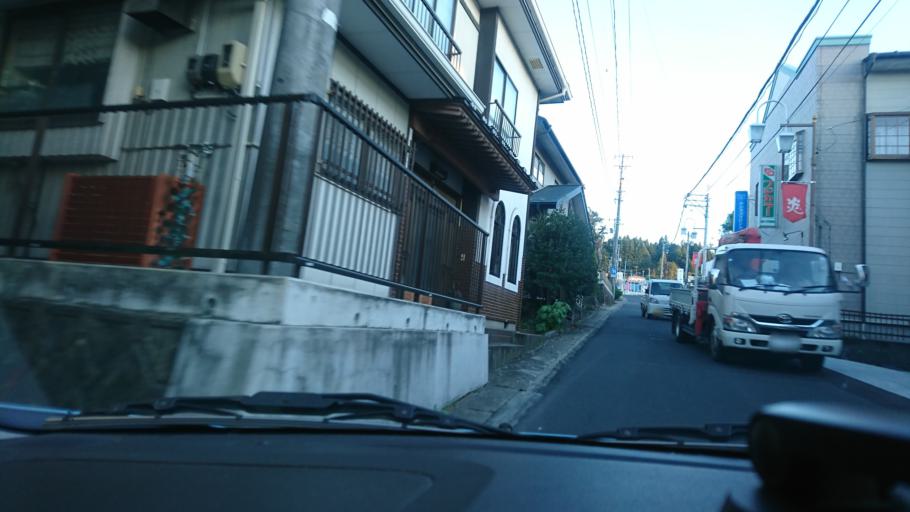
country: JP
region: Iwate
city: Ichinoseki
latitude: 38.8598
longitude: 141.3476
